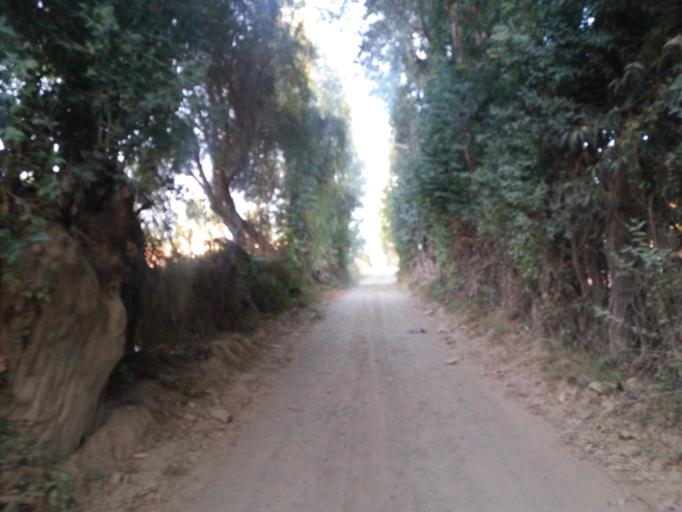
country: BO
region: Cochabamba
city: Cochabamba
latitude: -17.3533
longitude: -66.2140
